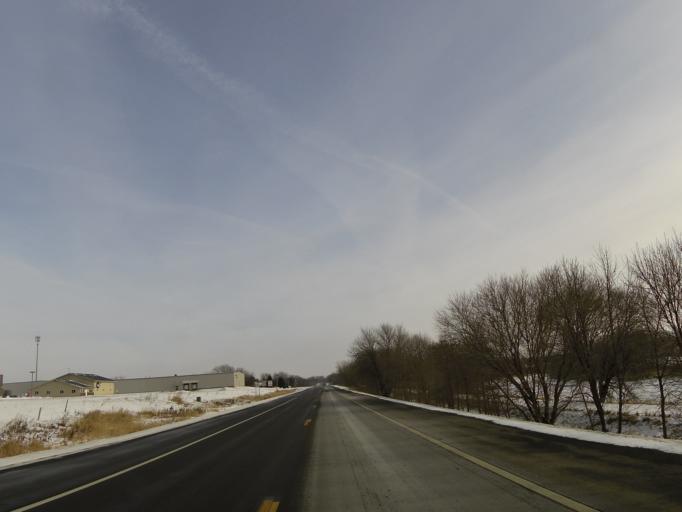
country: US
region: Minnesota
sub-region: McLeod County
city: Hutchinson
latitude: 44.8936
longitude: -94.4195
